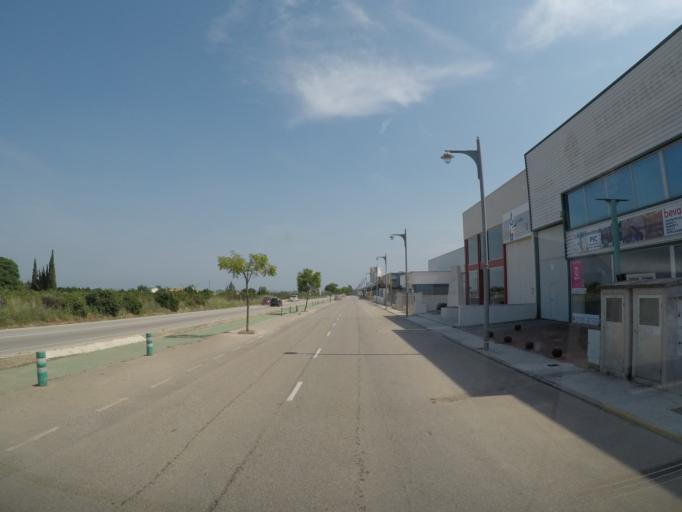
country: ES
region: Valencia
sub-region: Provincia de Alicante
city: Pego
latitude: 38.8447
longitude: -0.1011
